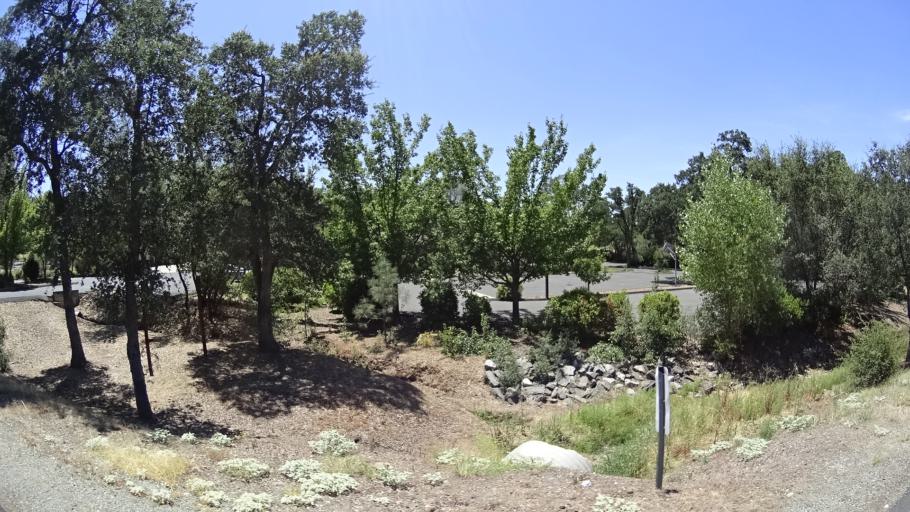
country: US
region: California
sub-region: Calaveras County
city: Rancho Calaveras
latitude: 38.1405
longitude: -120.8625
